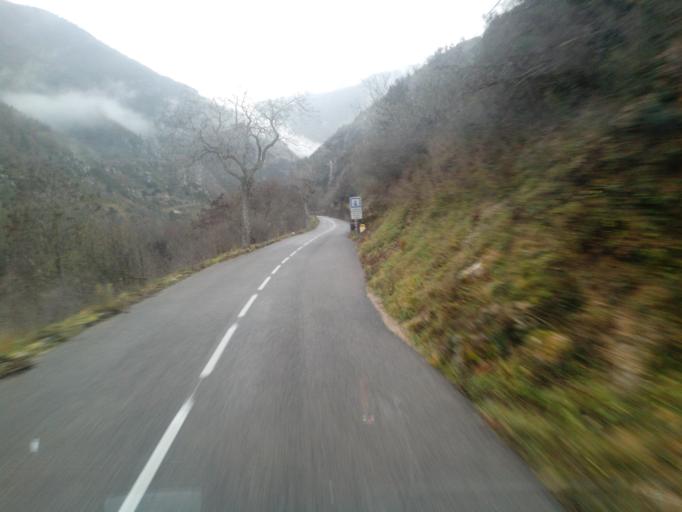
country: FR
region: Languedoc-Roussillon
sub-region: Departement de la Lozere
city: Chanac
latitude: 44.3064
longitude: 3.3286
